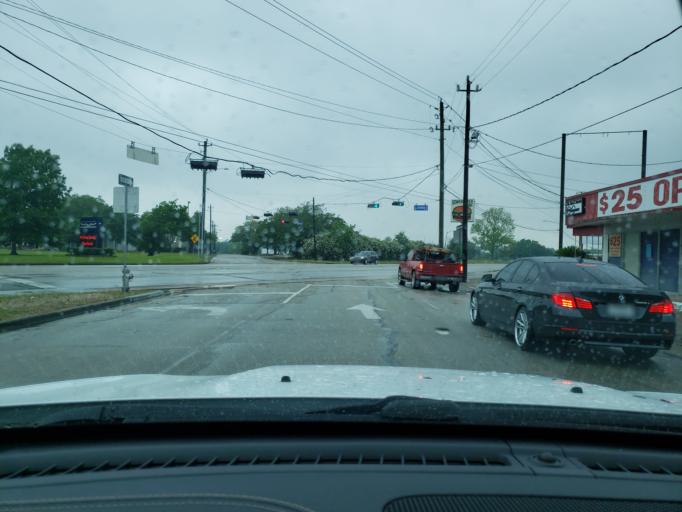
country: US
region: Texas
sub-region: Harris County
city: Baytown
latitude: 29.7370
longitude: -94.9778
